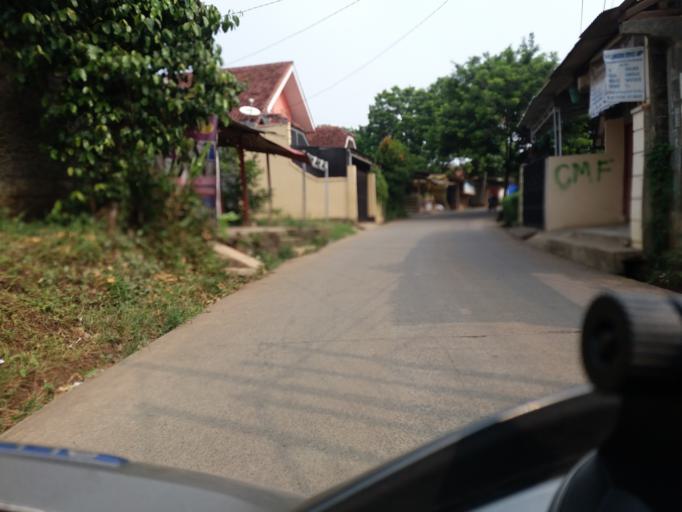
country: ID
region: West Java
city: Cibinong
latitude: -6.4388
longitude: 106.8641
